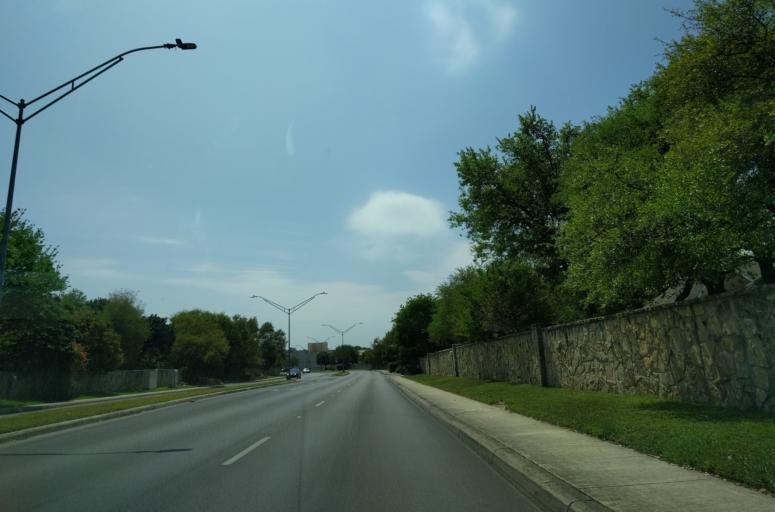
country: US
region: Texas
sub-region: Bexar County
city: Shavano Park
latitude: 29.5683
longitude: -98.5861
